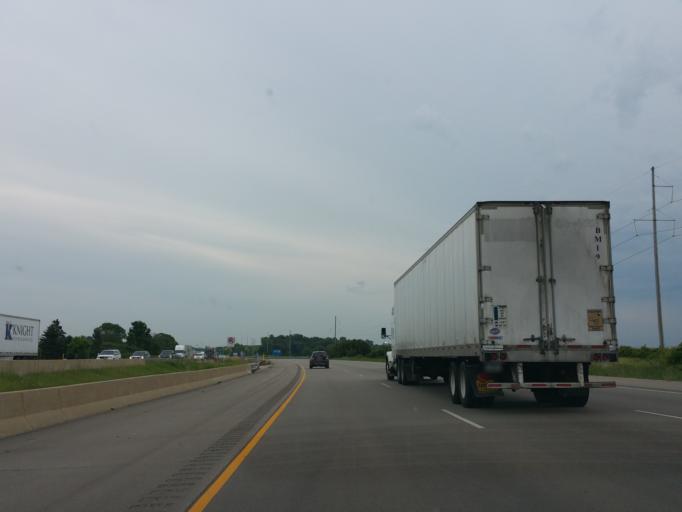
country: US
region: Wisconsin
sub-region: Dane County
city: Windsor
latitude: 43.2097
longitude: -89.3587
